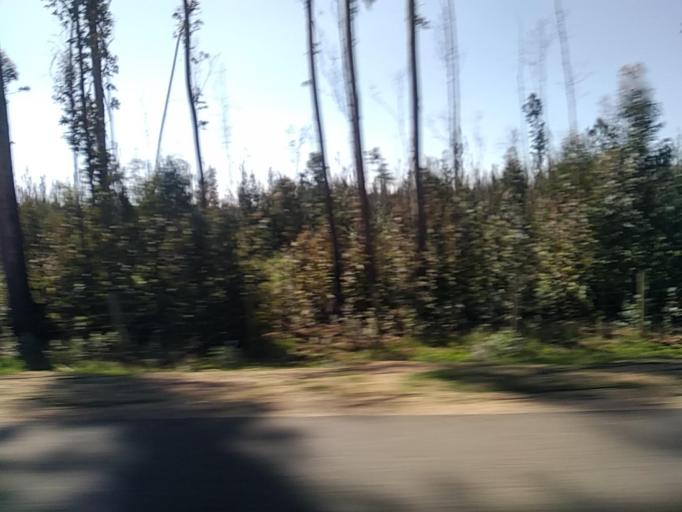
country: CL
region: Valparaiso
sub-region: San Antonio Province
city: El Tabo
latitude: -33.4032
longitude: -71.5740
